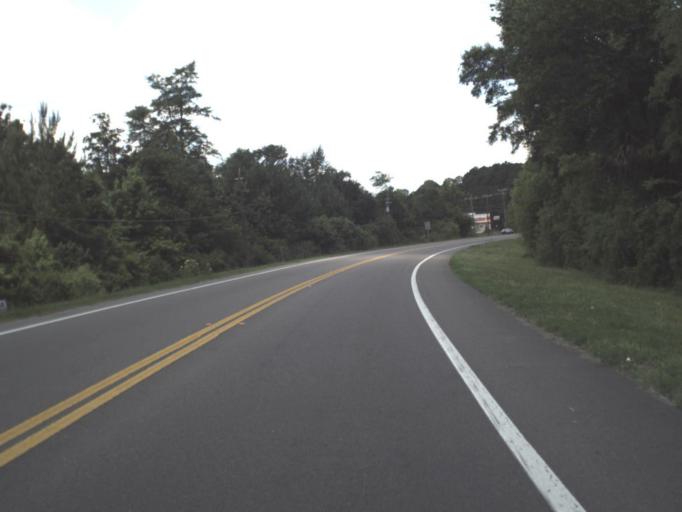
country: US
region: Florida
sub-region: Nassau County
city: Callahan
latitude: 30.5597
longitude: -81.8212
